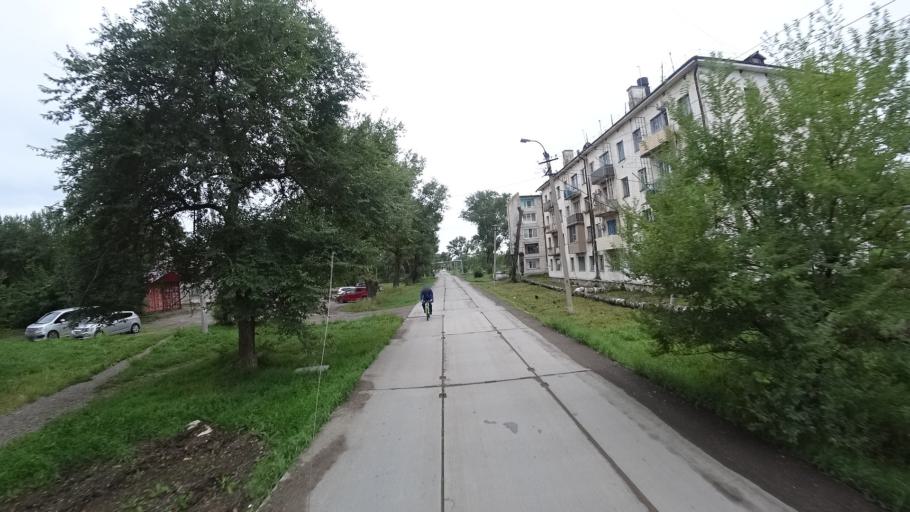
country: RU
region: Primorskiy
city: Chernigovka
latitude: 44.3338
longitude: 132.5370
